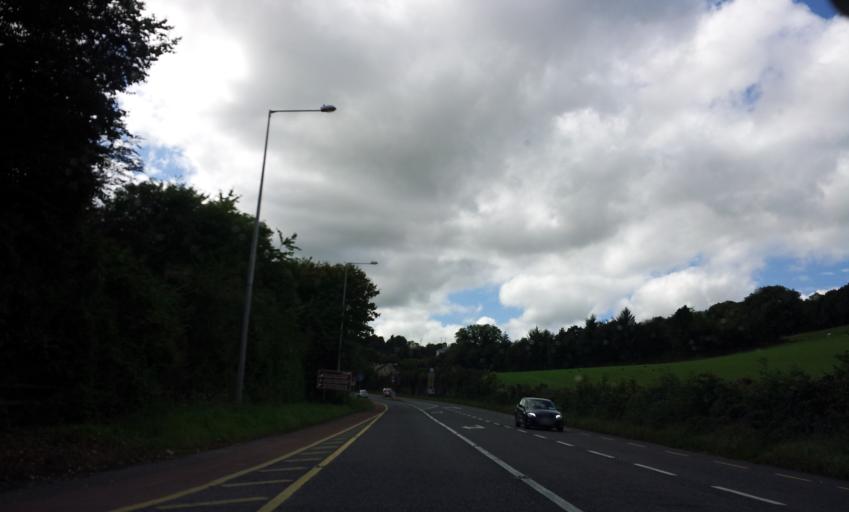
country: IE
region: Munster
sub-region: County Cork
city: Killumney
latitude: 51.8828
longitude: -8.6726
